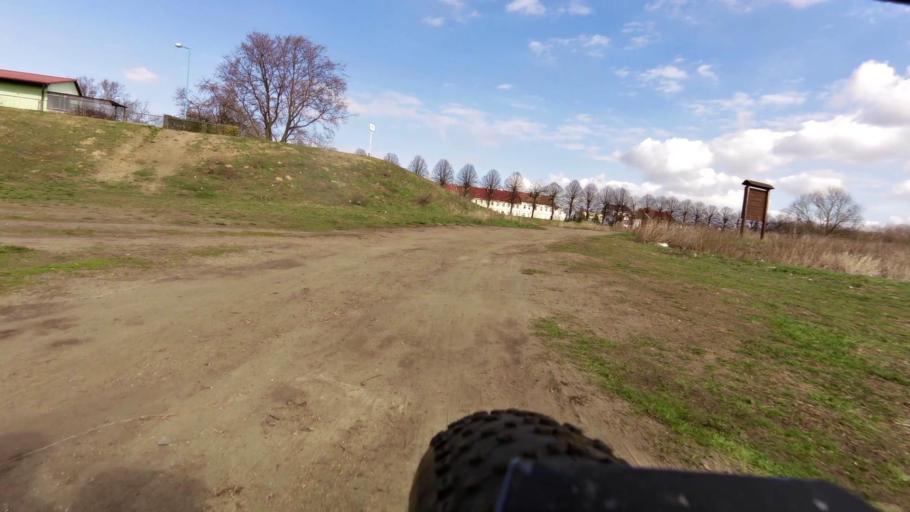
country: PL
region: Lubusz
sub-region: Powiat slubicki
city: Slubice
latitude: 52.3463
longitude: 14.5671
